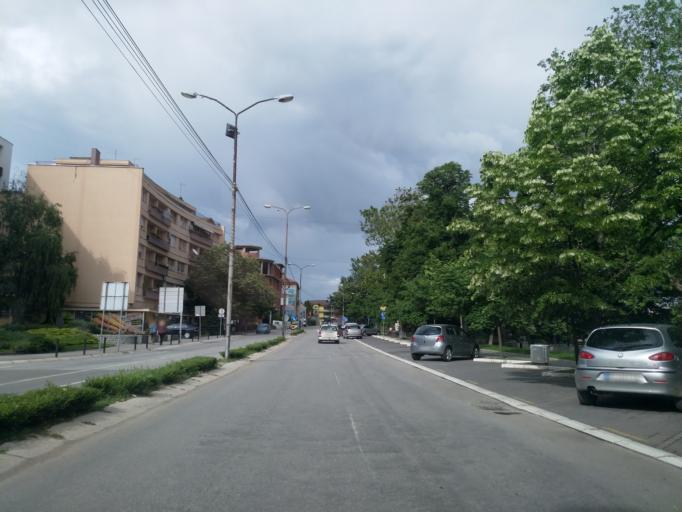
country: RS
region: Central Serbia
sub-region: Pomoravski Okrug
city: Paracin
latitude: 43.8634
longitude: 21.4102
